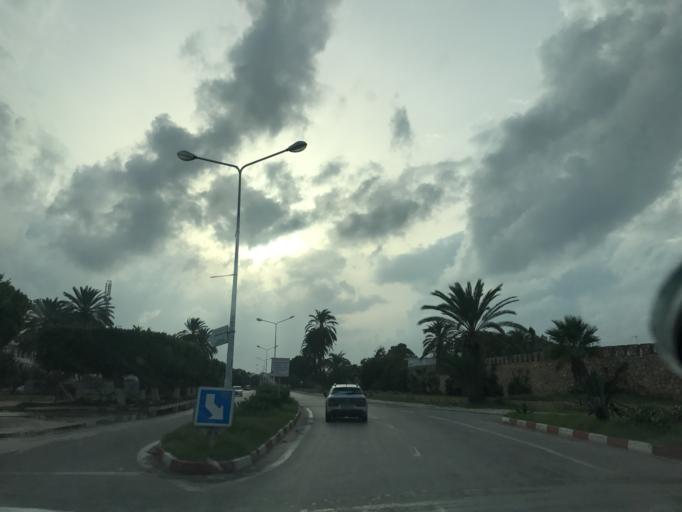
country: TN
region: Al Munastir
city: Saqanis
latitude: 35.7774
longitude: 10.7877
